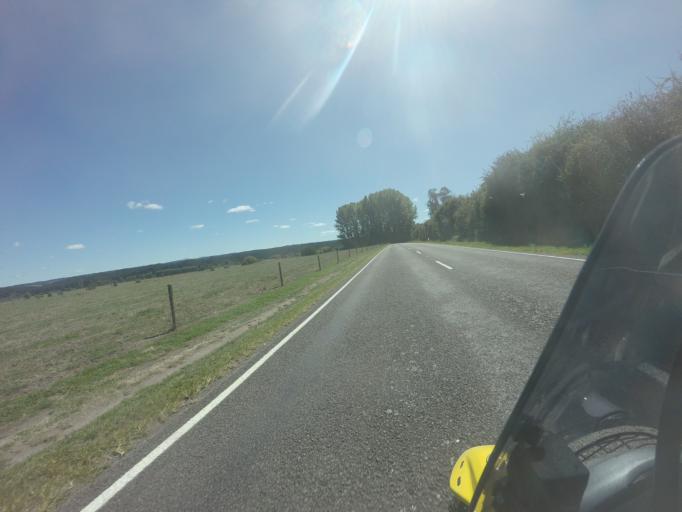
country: NZ
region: Bay of Plenty
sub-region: Whakatane District
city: Murupara
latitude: -38.3335
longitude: 176.7952
